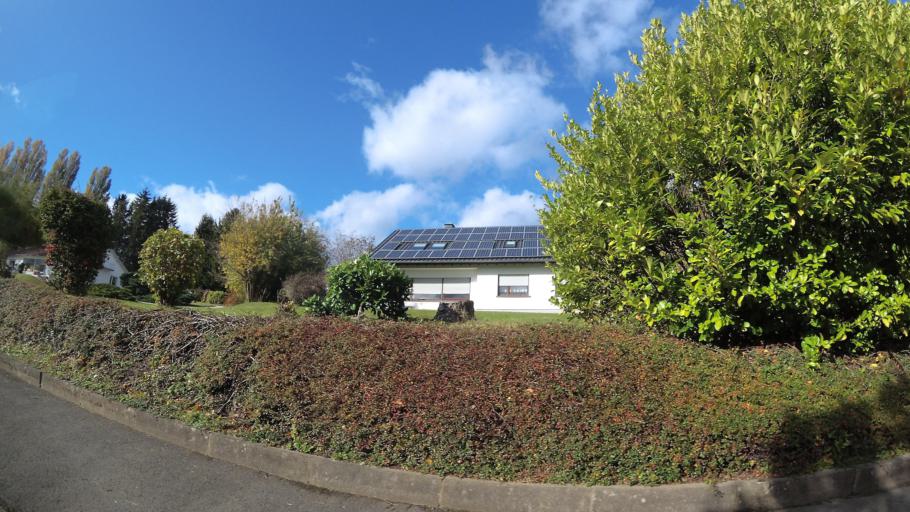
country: DE
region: Saarland
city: Blieskastel
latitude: 49.2343
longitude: 7.2449
